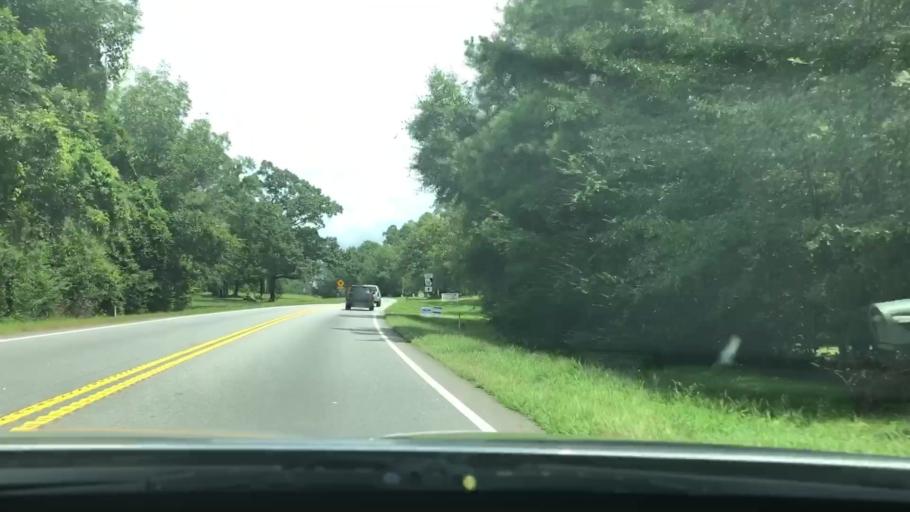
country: US
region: Georgia
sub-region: Lamar County
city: Barnesville
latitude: 33.1532
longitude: -84.1373
